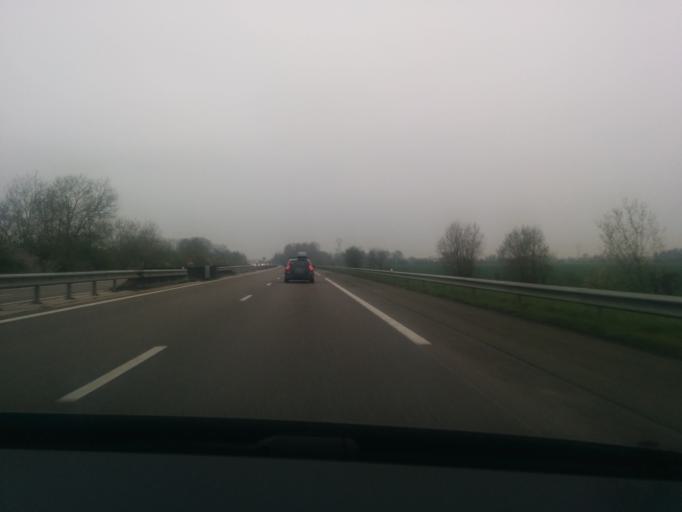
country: FR
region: Bourgogne
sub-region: Departement de la Cote-d'Or
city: Genlis
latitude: 47.2649
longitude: 5.1980
